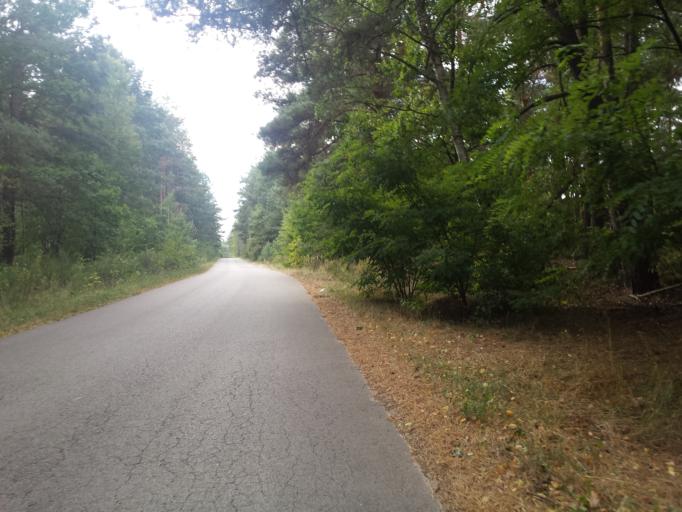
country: PL
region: Swietokrzyskie
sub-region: Powiat kielecki
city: Rakow
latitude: 50.6774
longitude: 21.0696
